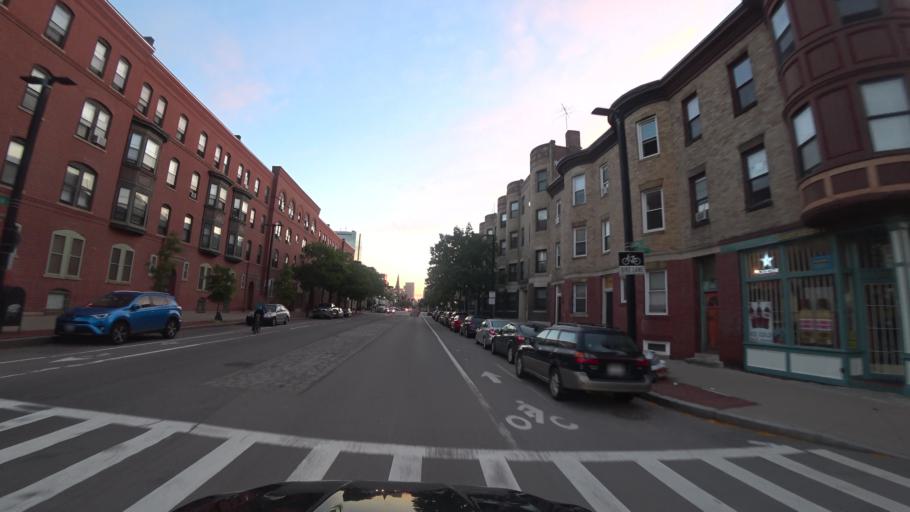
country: US
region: Massachusetts
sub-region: Suffolk County
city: Boston
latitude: 42.3391
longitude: -71.0836
